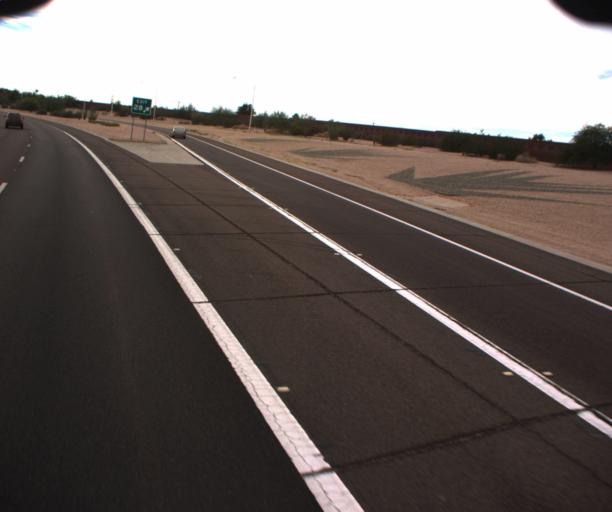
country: US
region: Arizona
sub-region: Pinal County
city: Apache Junction
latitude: 33.4126
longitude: -111.6391
